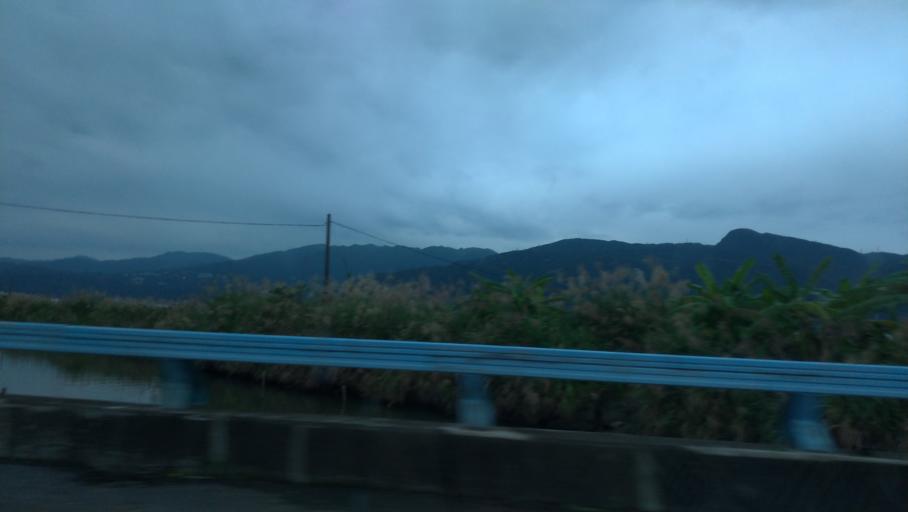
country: TW
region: Taiwan
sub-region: Yilan
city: Yilan
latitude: 24.8230
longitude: 121.7987
